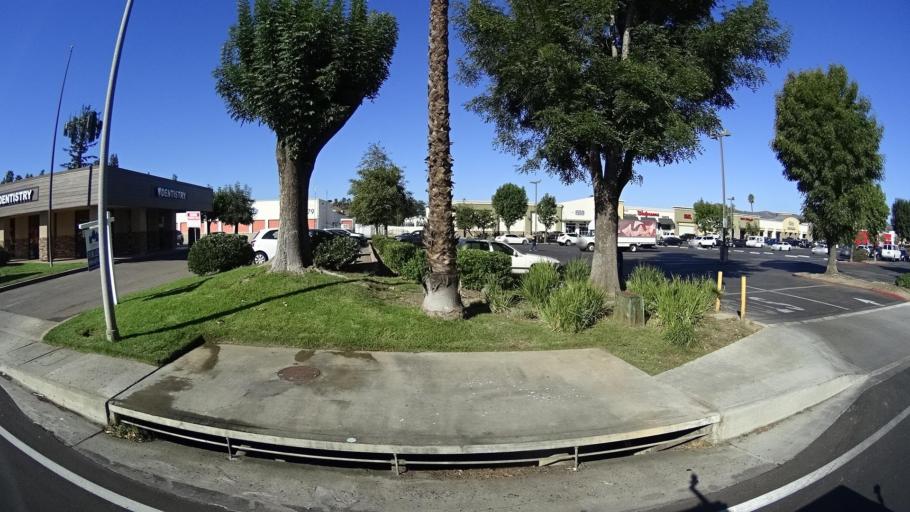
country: US
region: California
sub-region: San Diego County
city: Lakeside
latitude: 32.8543
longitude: -116.9312
